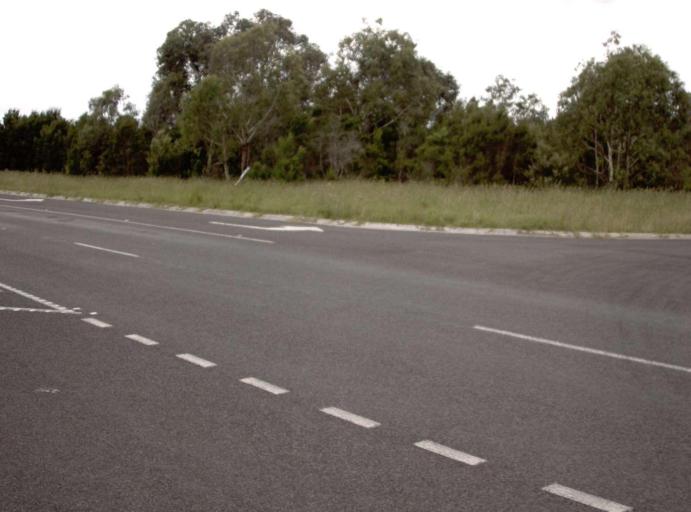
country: AU
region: Victoria
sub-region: Bass Coast
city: North Wonthaggi
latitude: -38.3711
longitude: 145.6847
